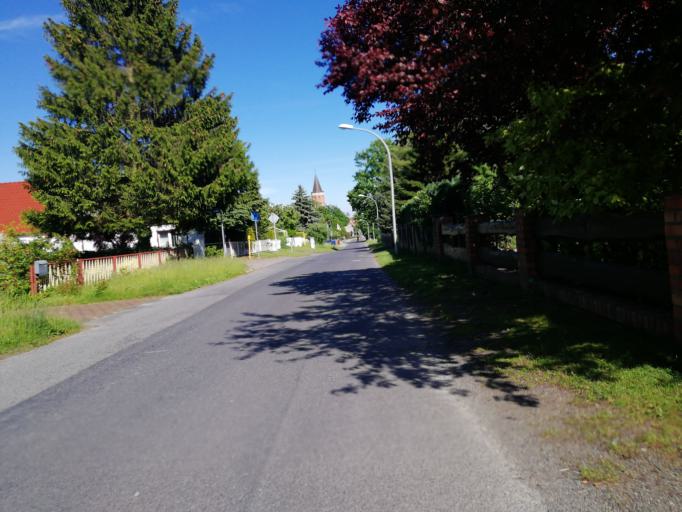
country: DE
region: Brandenburg
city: Calau
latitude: 51.7461
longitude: 13.9414
